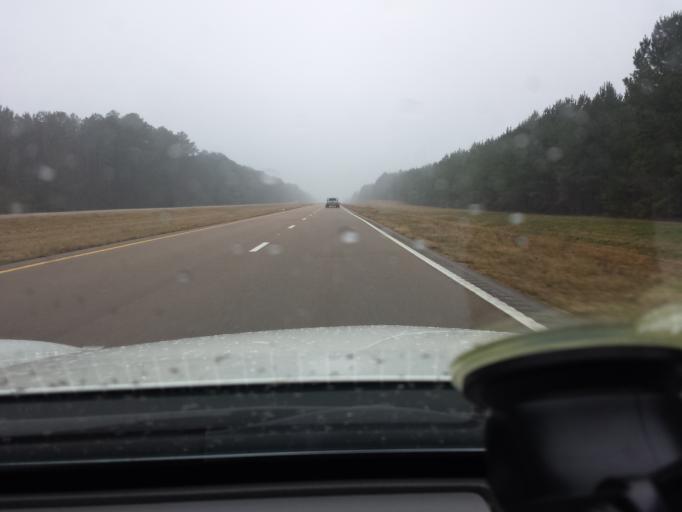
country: US
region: Mississippi
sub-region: Scott County
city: Morton
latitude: 32.5532
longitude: -89.7672
